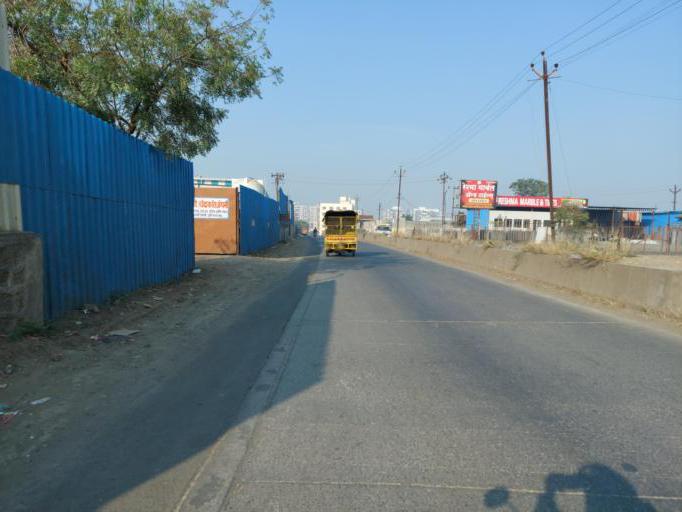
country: IN
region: Maharashtra
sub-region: Pune Division
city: Pune
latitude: 18.4572
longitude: 73.9419
